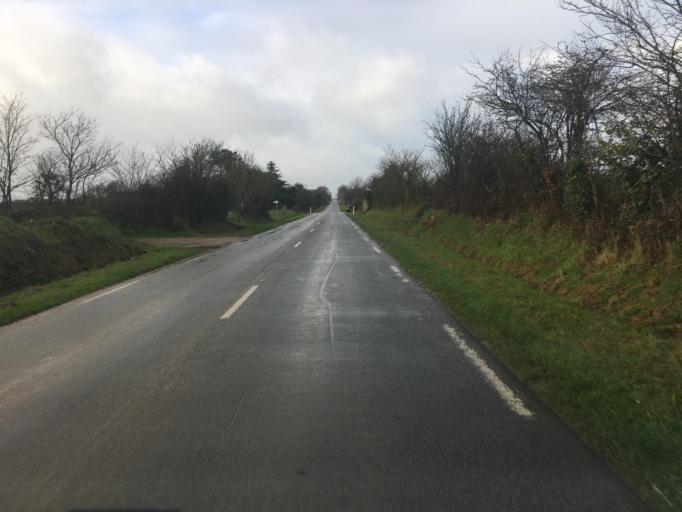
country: FR
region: Lower Normandy
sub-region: Departement de la Manche
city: Saint-Pierre-Eglise
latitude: 49.6693
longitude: -1.3622
